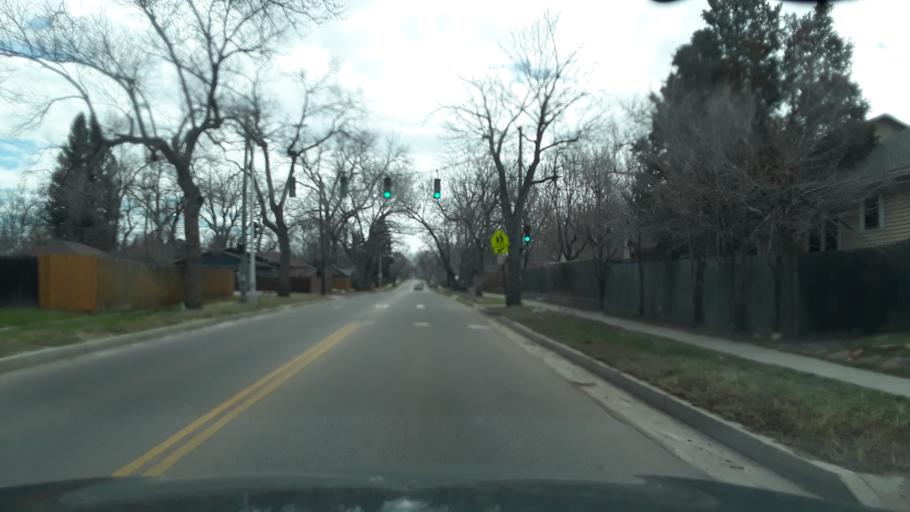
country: US
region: Colorado
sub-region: El Paso County
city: Colorado Springs
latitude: 38.8501
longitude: -104.8074
